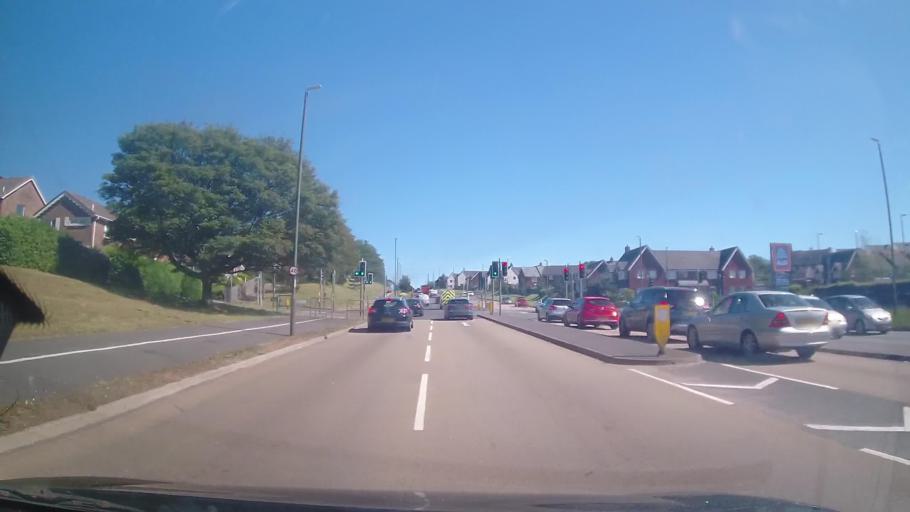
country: GB
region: England
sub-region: Borough of Torbay
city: Paignton
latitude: 50.4198
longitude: -3.5852
